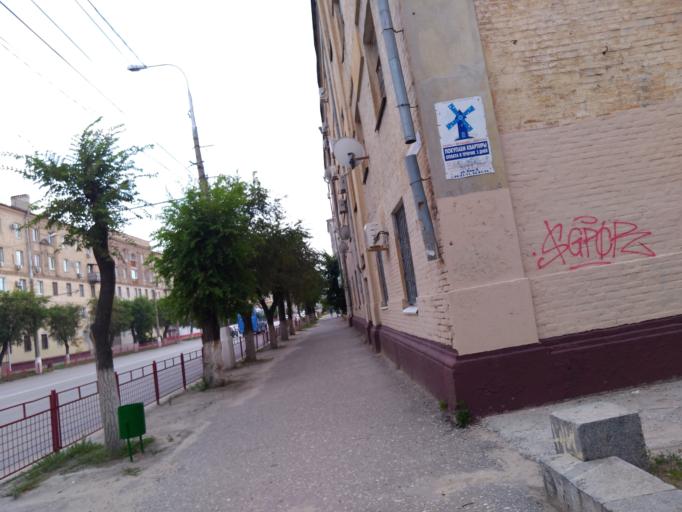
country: RU
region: Volgograd
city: Volgograd
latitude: 48.6927
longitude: 44.4923
